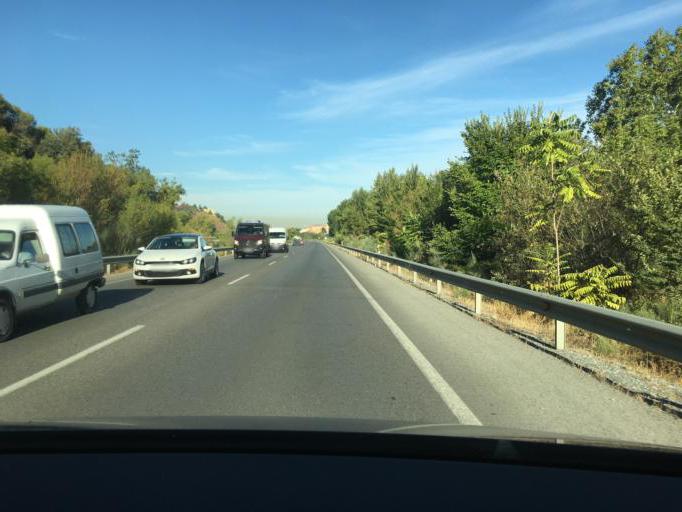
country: ES
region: Andalusia
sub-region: Provincia de Granada
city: Huetor Vega
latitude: 37.1594
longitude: -3.5563
